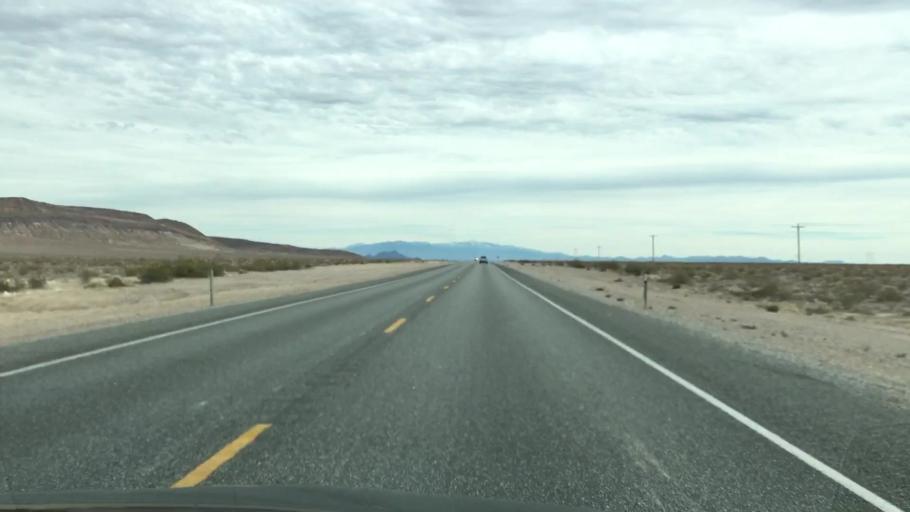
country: US
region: Nevada
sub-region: Nye County
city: Beatty
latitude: 36.6938
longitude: -116.5699
